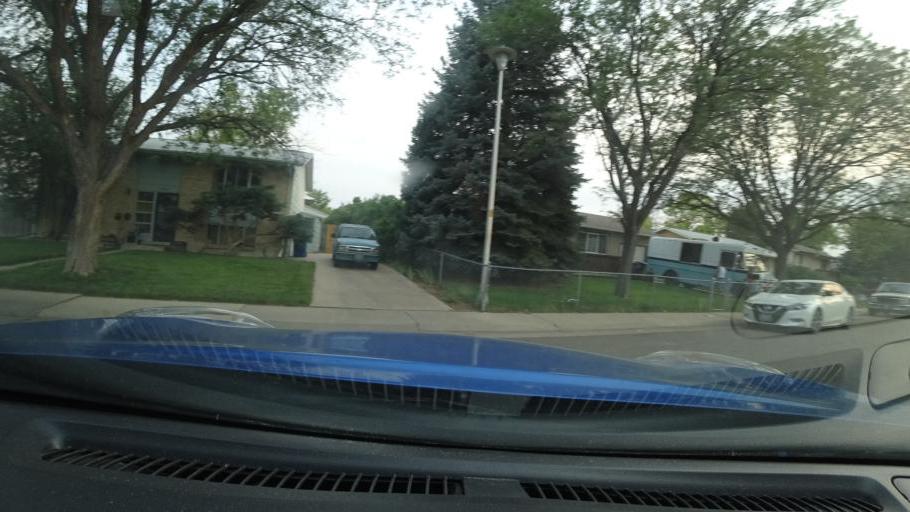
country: US
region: Colorado
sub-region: Adams County
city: Aurora
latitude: 39.7297
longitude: -104.7932
